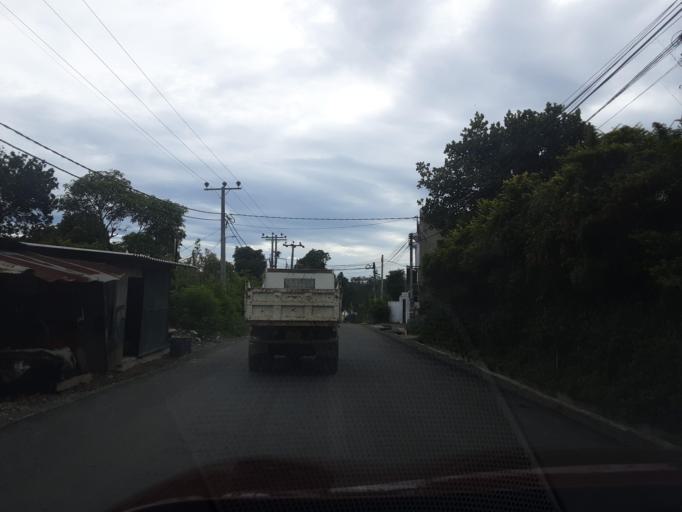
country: LK
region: Uva
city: Haputale
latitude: 6.8362
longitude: 80.9979
